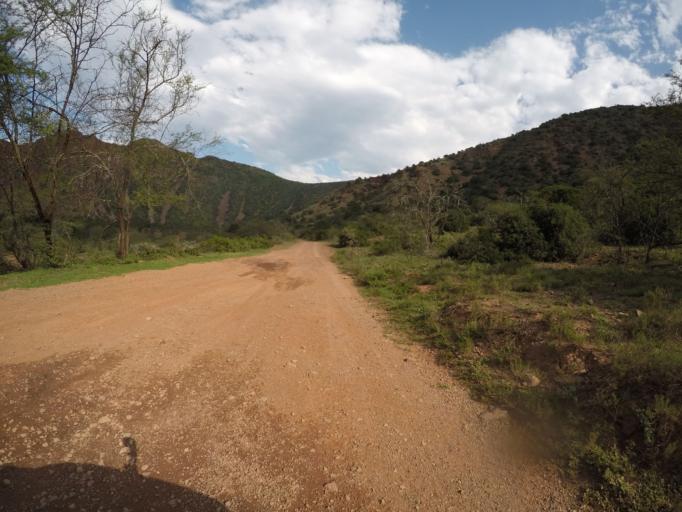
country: ZA
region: Eastern Cape
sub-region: Cacadu District Municipality
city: Kareedouw
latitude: -33.6376
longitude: 24.3165
